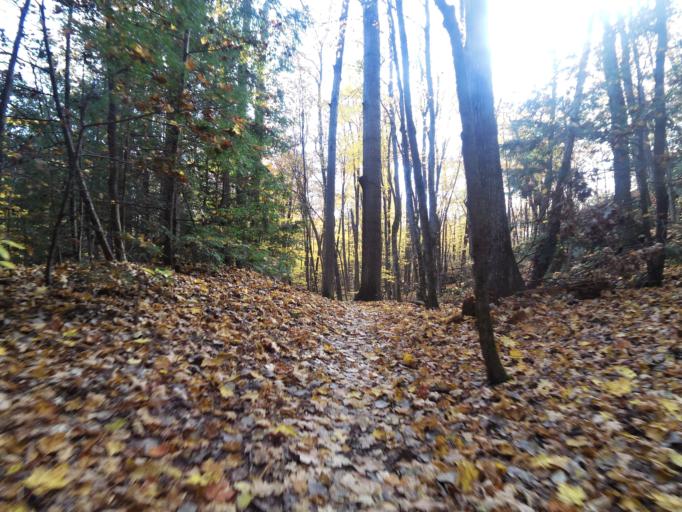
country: CA
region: Quebec
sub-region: Outaouais
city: Gatineau
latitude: 45.4883
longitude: -75.8146
